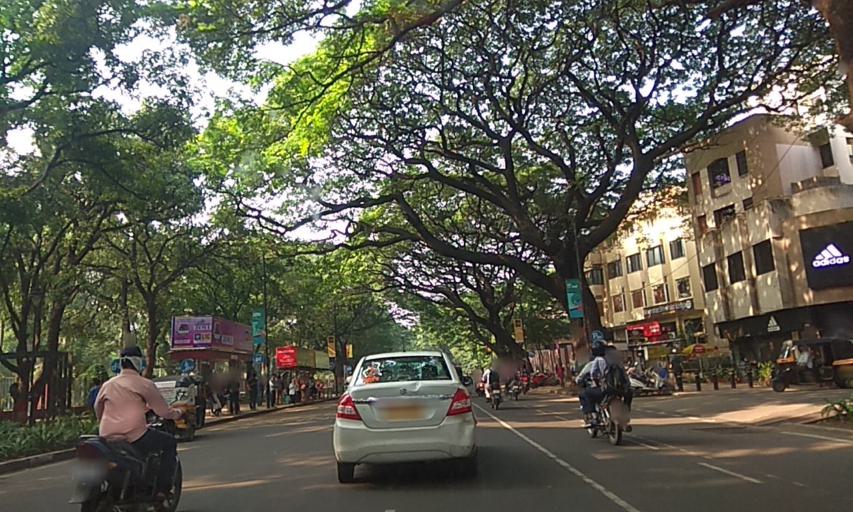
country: IN
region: Maharashtra
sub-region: Pune Division
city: Pune
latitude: 18.5220
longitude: 73.8474
